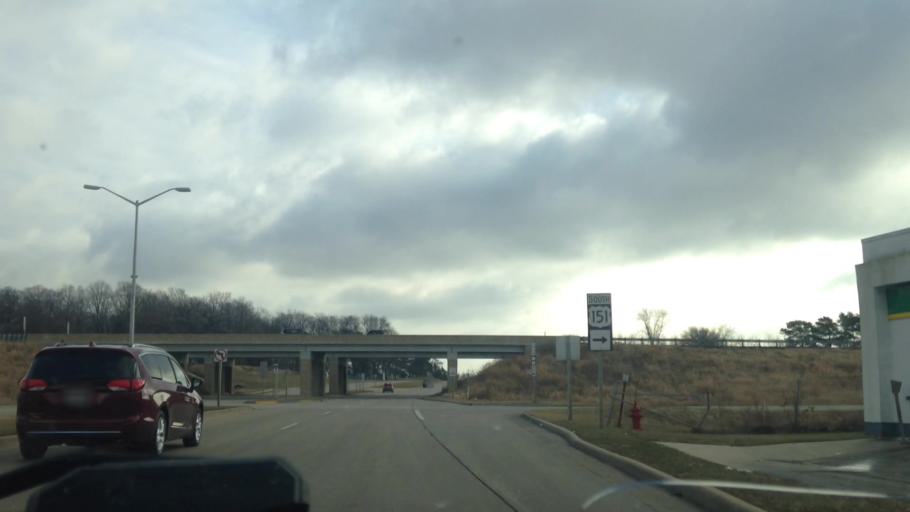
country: US
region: Wisconsin
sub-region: Dodge County
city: Beaver Dam
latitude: 43.4562
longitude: -88.8170
